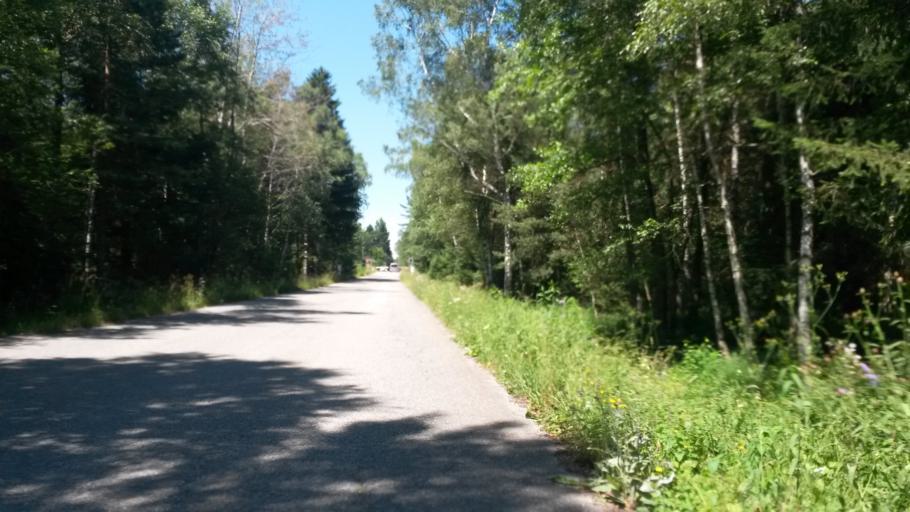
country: DE
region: Bavaria
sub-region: Upper Bavaria
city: Bernau am Chiemsee
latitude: 47.8125
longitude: 12.3981
